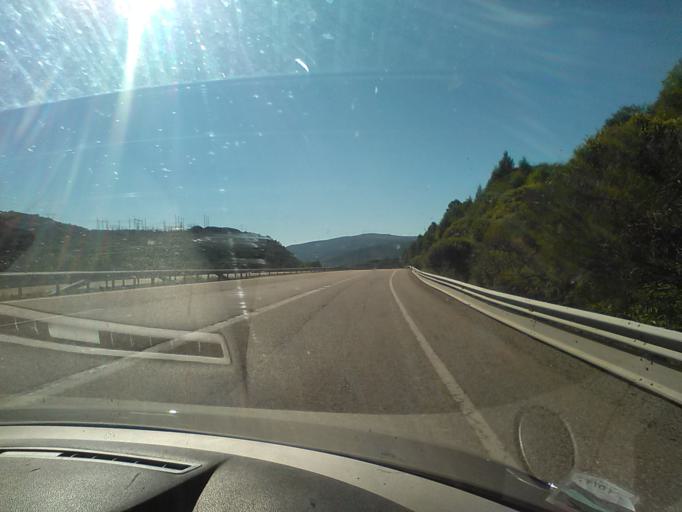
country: ES
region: Castille and Leon
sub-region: Provincia de Zamora
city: Lubian
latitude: 42.0347
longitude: -6.8523
